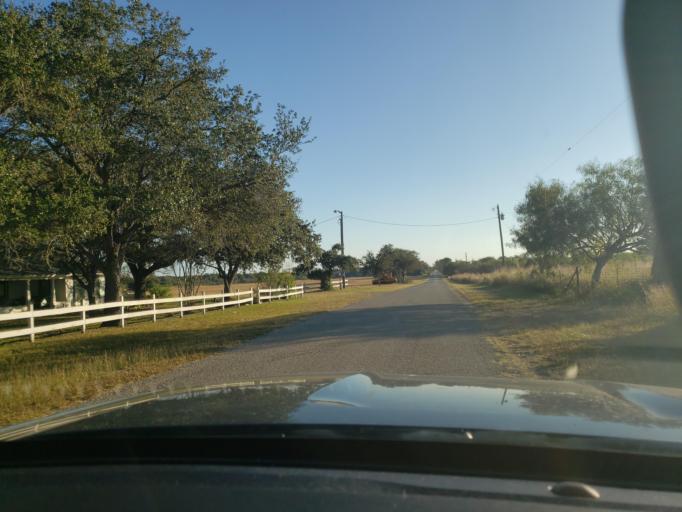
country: US
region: Texas
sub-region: Bee County
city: Beeville
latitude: 28.4209
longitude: -97.7114
